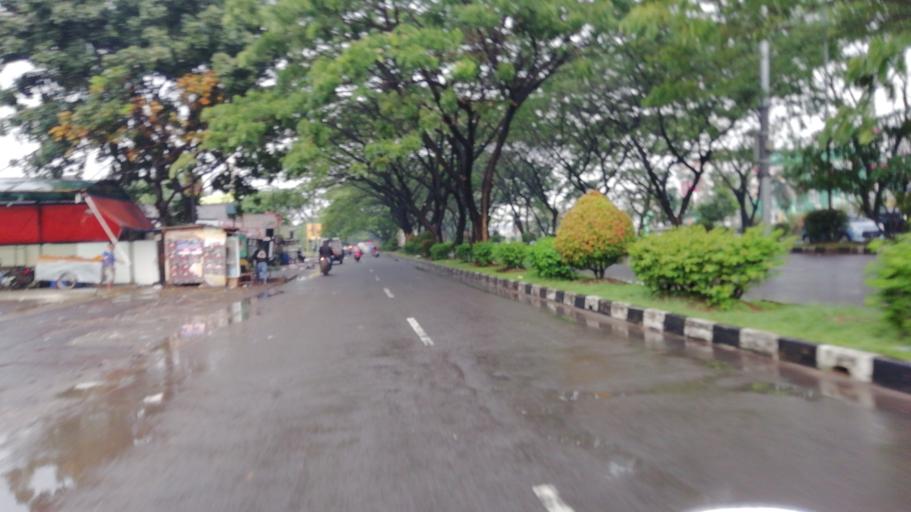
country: ID
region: West Java
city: Cibinong
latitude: -6.4818
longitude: 106.8112
